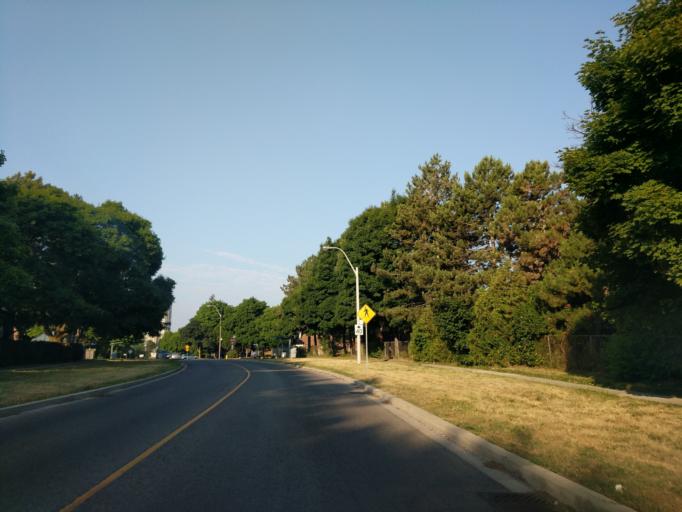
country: CA
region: Ontario
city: Willowdale
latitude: 43.8022
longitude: -79.3477
